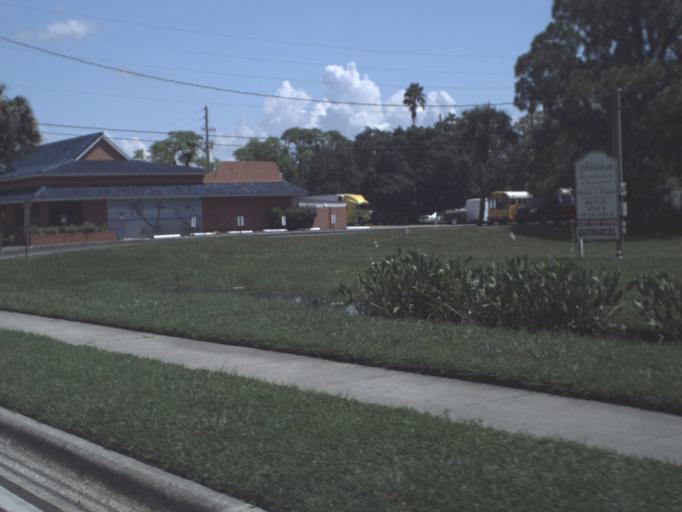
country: US
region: Florida
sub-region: Pinellas County
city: Gulfport
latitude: 27.7425
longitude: -82.6792
